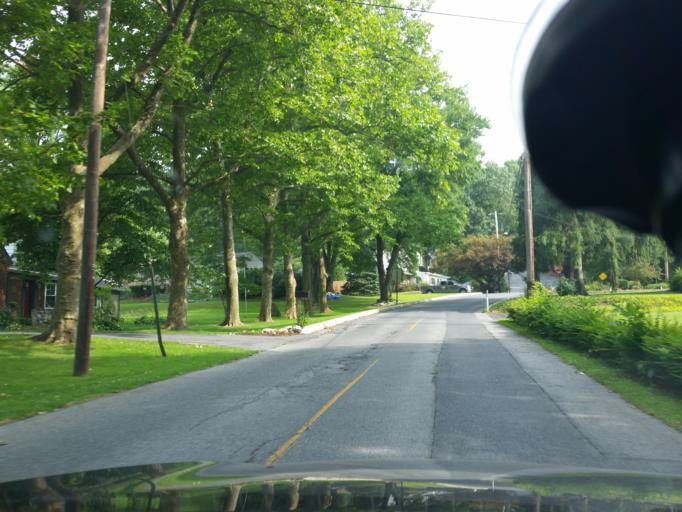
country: US
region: Pennsylvania
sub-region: Perry County
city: Marysville
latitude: 40.3351
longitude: -76.9350
